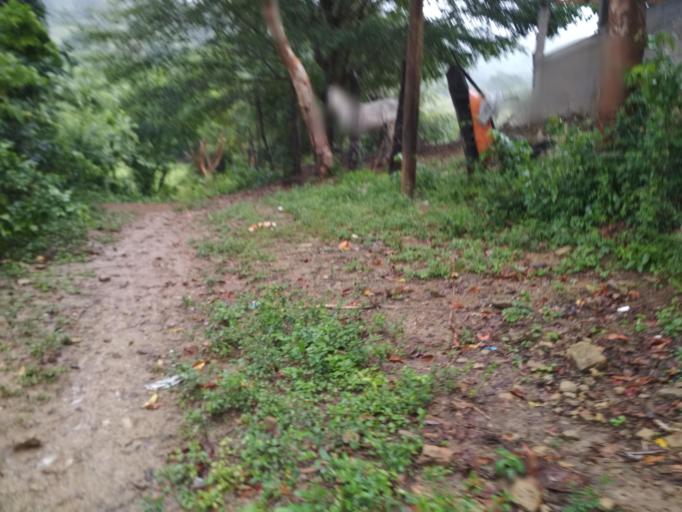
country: MX
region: Veracruz
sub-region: Chalma
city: San Pedro Coyutla
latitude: 21.1869
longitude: -98.4330
